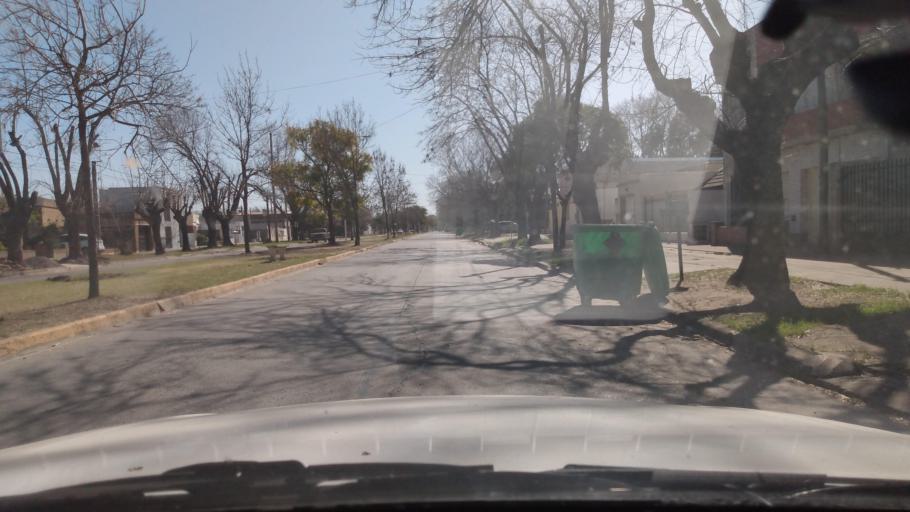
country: AR
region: Buenos Aires
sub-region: Partido de Mercedes
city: Mercedes
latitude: -34.6527
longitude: -59.4174
